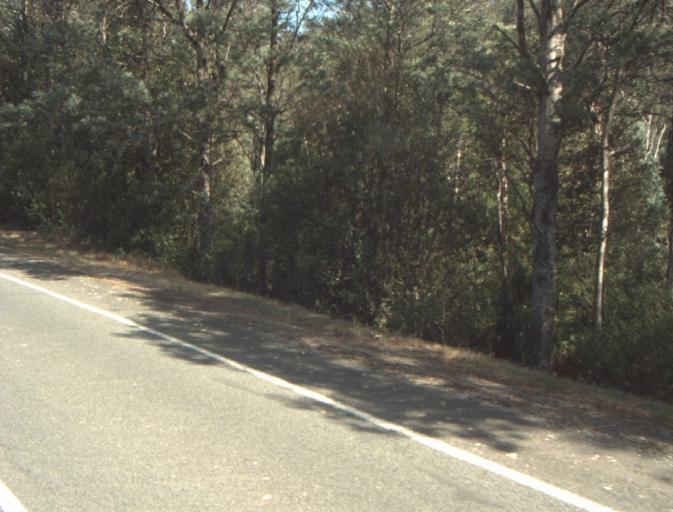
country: AU
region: Tasmania
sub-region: Launceston
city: Mayfield
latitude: -41.2705
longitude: 147.2145
